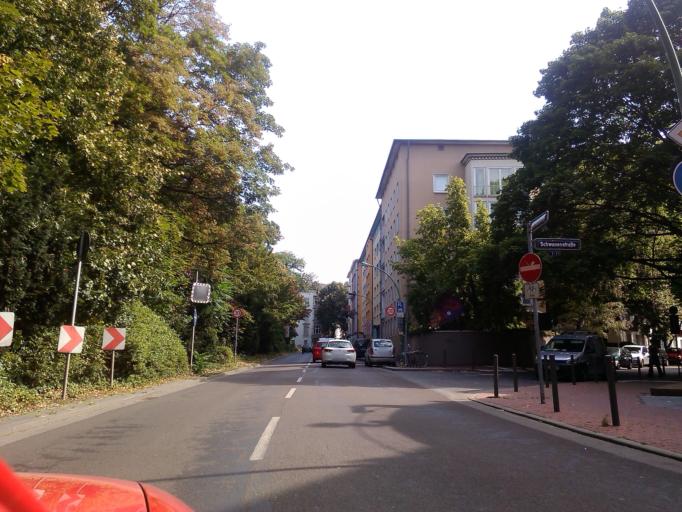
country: DE
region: Hesse
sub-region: Regierungsbezirk Darmstadt
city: Frankfurt am Main
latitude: 50.1112
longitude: 8.6945
